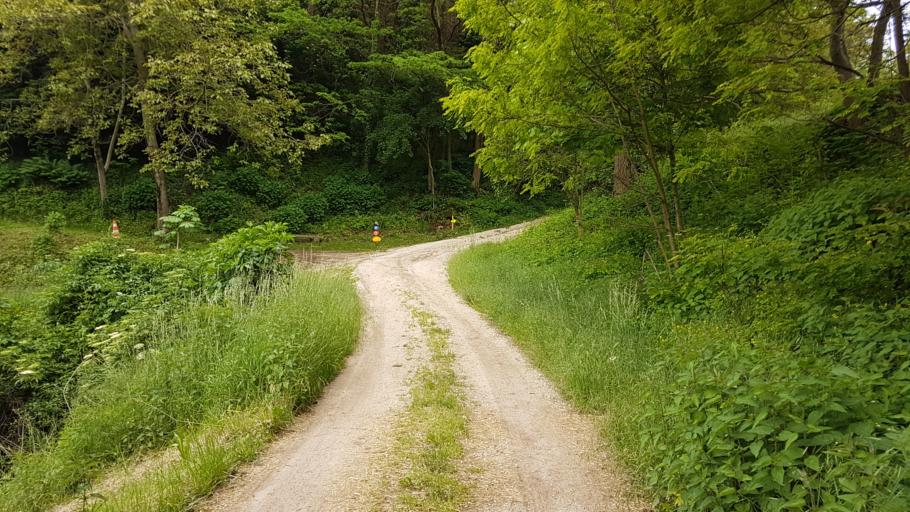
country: IT
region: Veneto
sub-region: Provincia di Vicenza
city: Nogarole Vicentino
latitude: 45.5497
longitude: 11.3150
